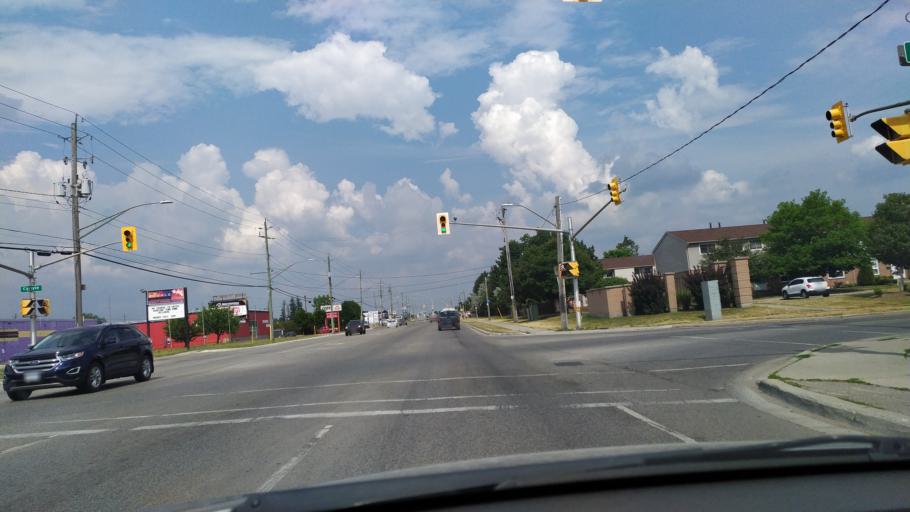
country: CA
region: Ontario
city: London
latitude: 43.0084
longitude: -81.1623
